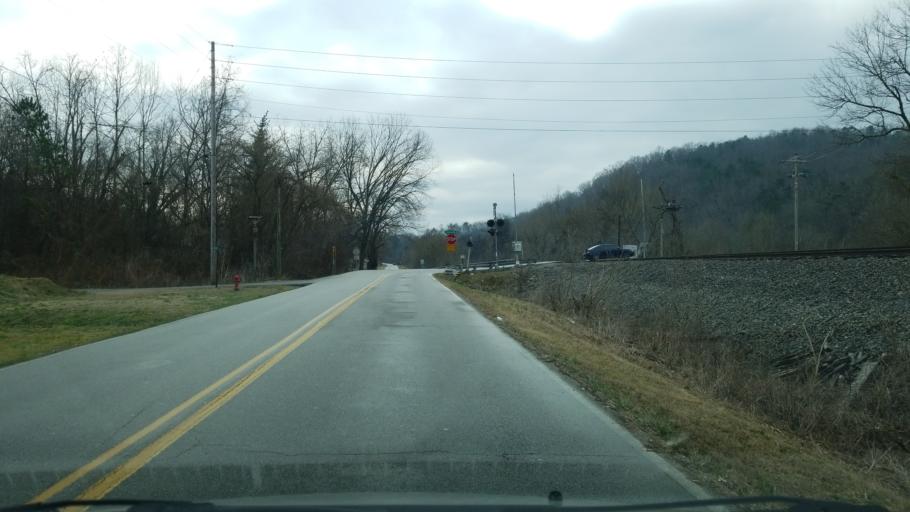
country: US
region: Tennessee
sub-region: Hamilton County
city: East Brainerd
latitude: 34.9783
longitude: -85.1439
